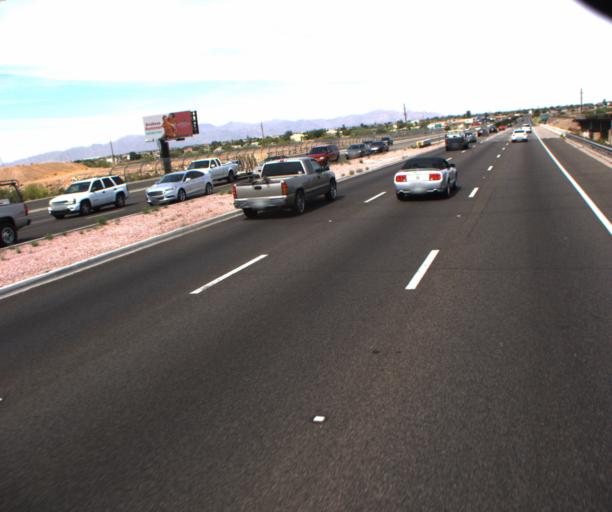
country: US
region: Arizona
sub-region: Maricopa County
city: Youngtown
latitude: 33.6066
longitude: -112.3032
